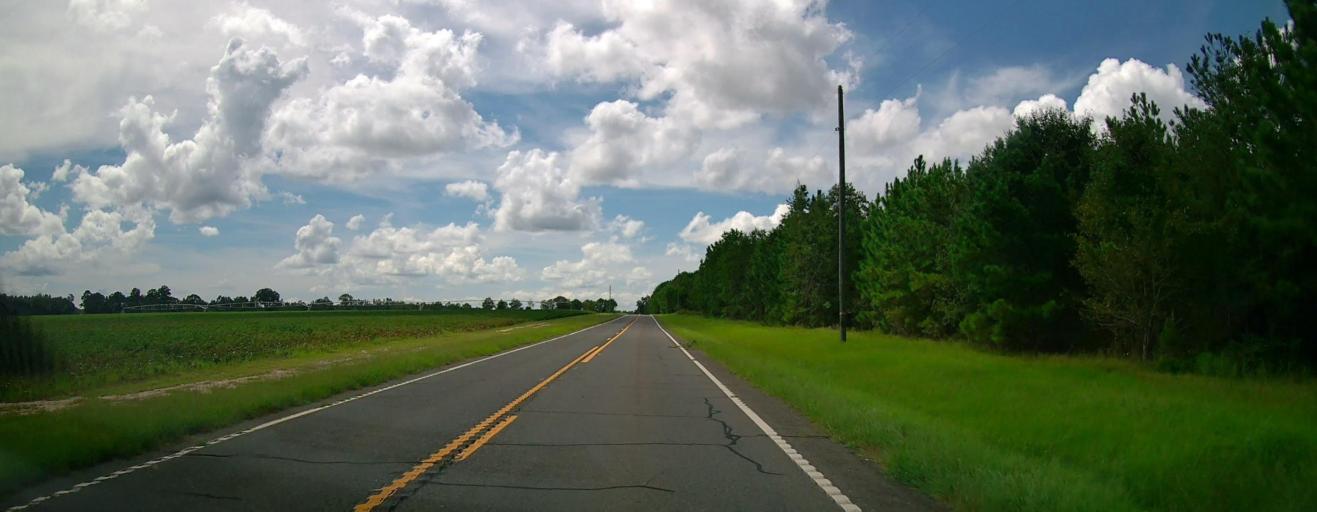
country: US
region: Georgia
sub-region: Macon County
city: Marshallville
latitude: 32.4335
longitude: -84.0596
